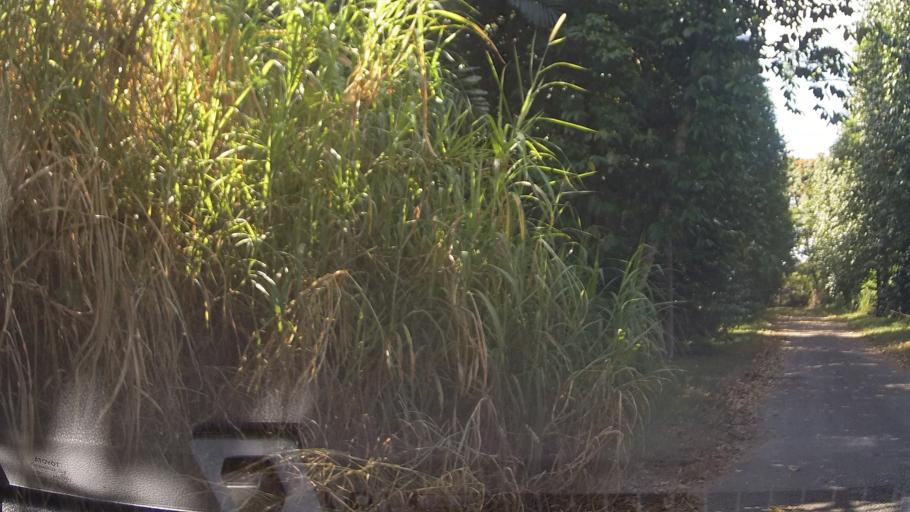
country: MY
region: Johor
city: Johor Bahru
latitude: 1.4398
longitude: 103.7098
